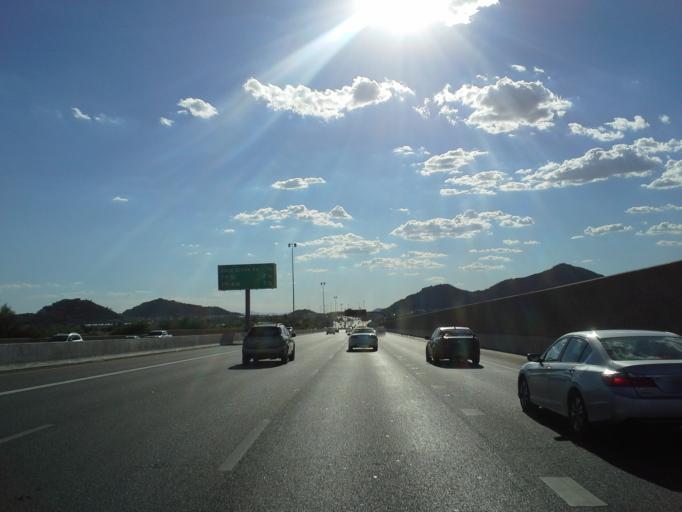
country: US
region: Arizona
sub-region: Maricopa County
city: Paradise Valley
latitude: 33.6729
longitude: -112.0143
